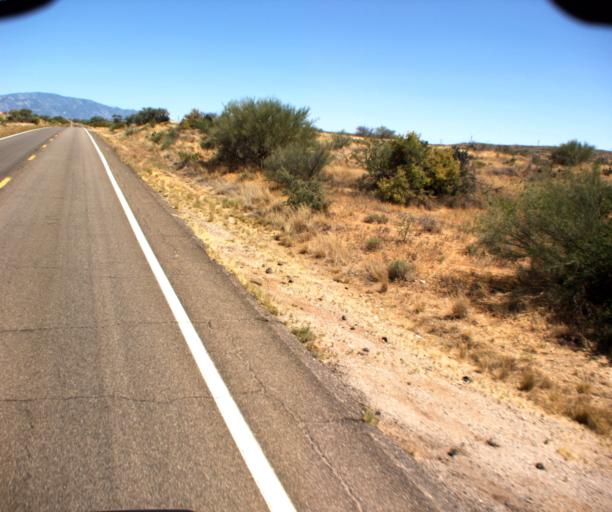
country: US
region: Arizona
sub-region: Pima County
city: Catalina
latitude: 32.6281
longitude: -111.0021
